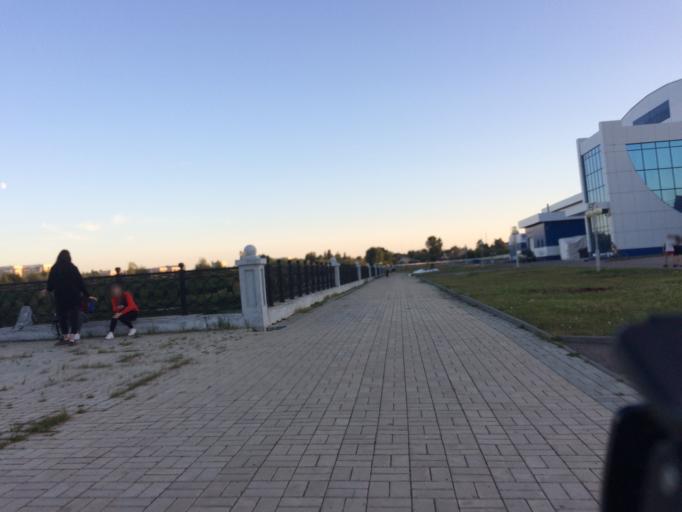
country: RU
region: Mariy-El
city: Yoshkar-Ola
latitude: 56.6250
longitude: 47.8963
